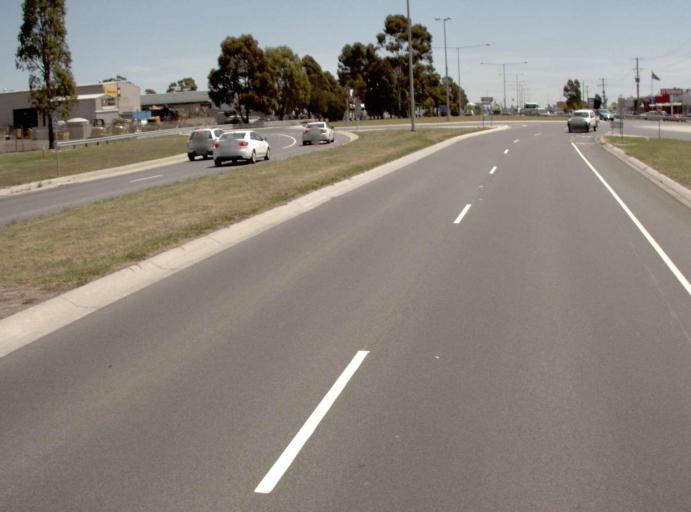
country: AU
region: Victoria
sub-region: Latrobe
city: Traralgon
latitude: -38.1897
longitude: 146.5672
